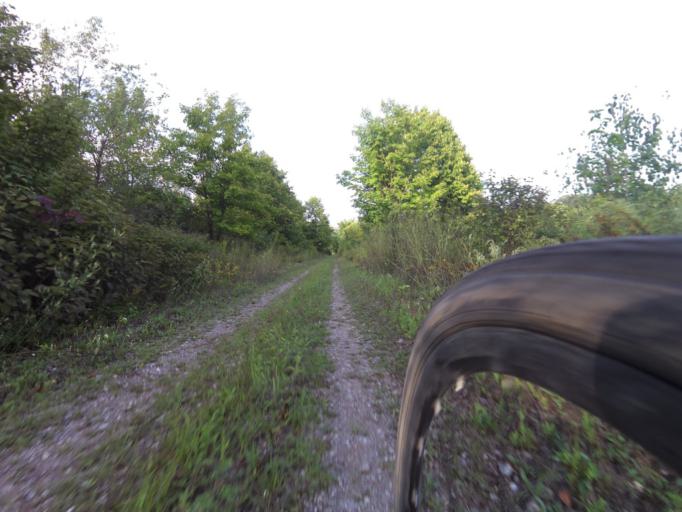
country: CA
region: Ontario
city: Gananoque
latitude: 44.5409
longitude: -76.4010
